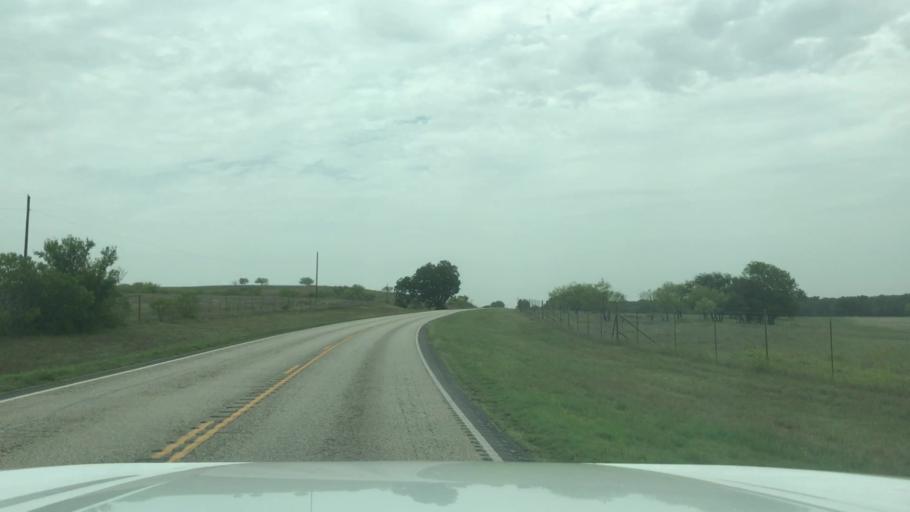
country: US
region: Texas
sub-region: Erath County
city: Dublin
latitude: 32.0573
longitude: -98.1871
